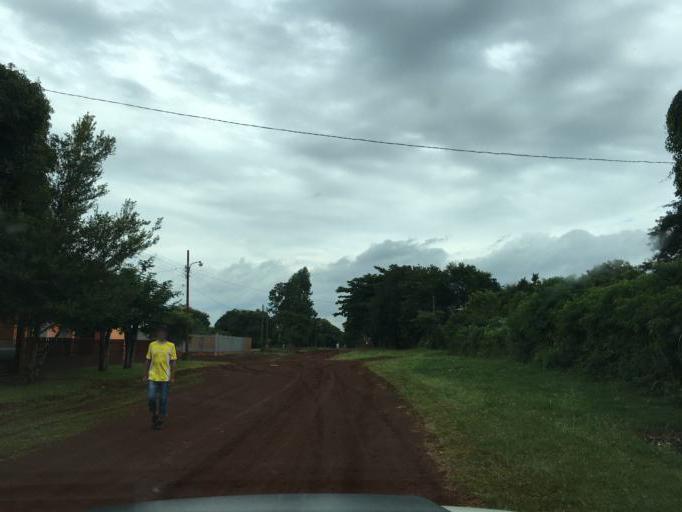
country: PY
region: Alto Parana
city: Ciudad del Este
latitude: -25.4184
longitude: -54.6451
